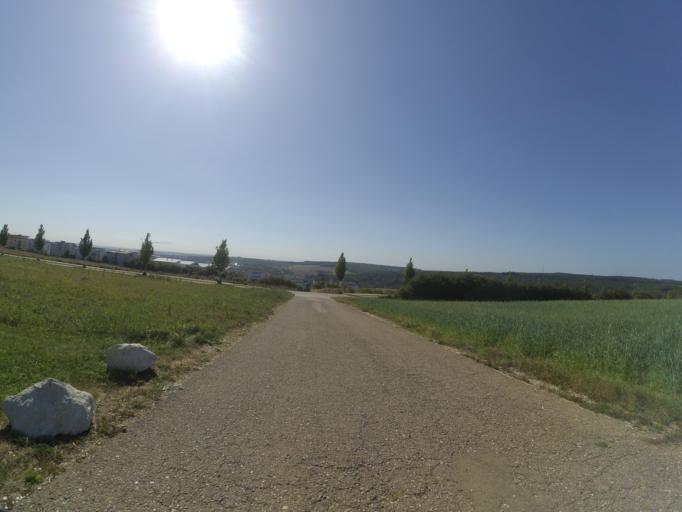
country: DE
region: Baden-Wuerttemberg
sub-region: Tuebingen Region
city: Dornstadt
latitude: 48.4179
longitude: 9.9379
